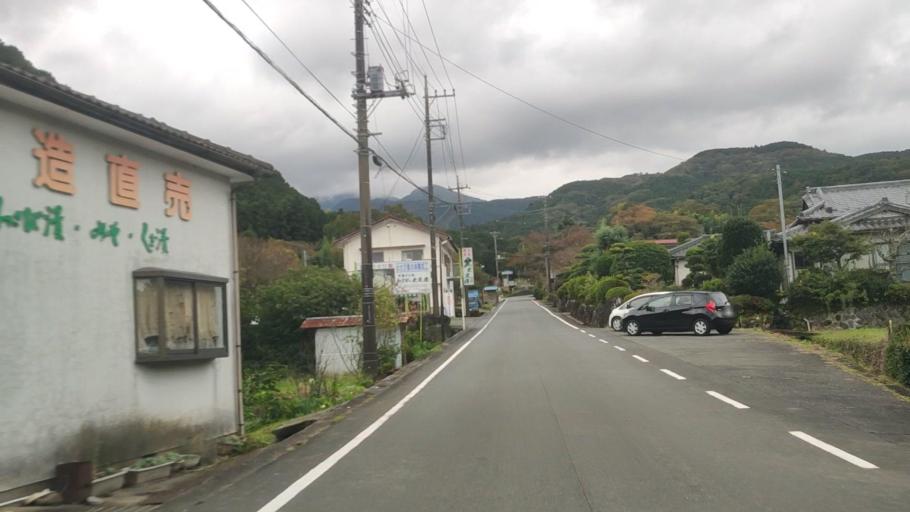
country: JP
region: Shizuoka
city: Ito
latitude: 34.9156
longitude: 138.9924
